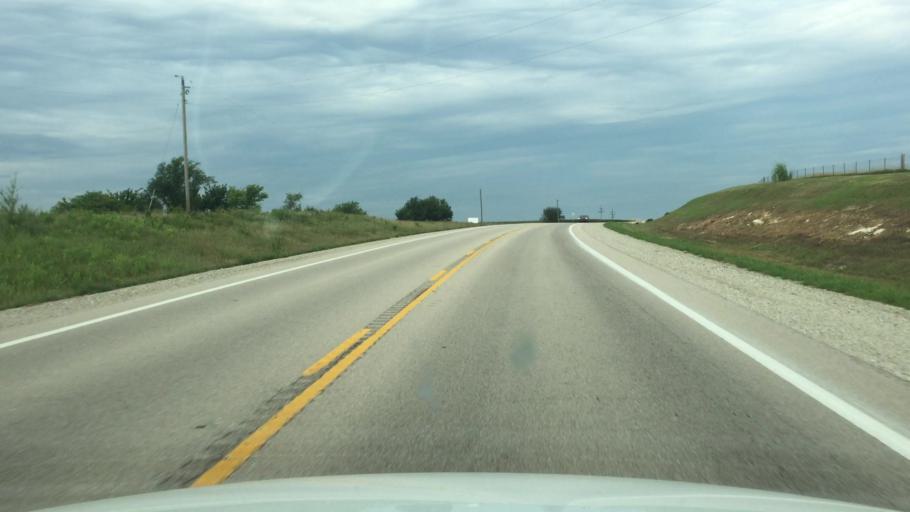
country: US
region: Kansas
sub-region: Nemaha County
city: Sabetha
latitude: 39.8420
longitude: -95.6897
